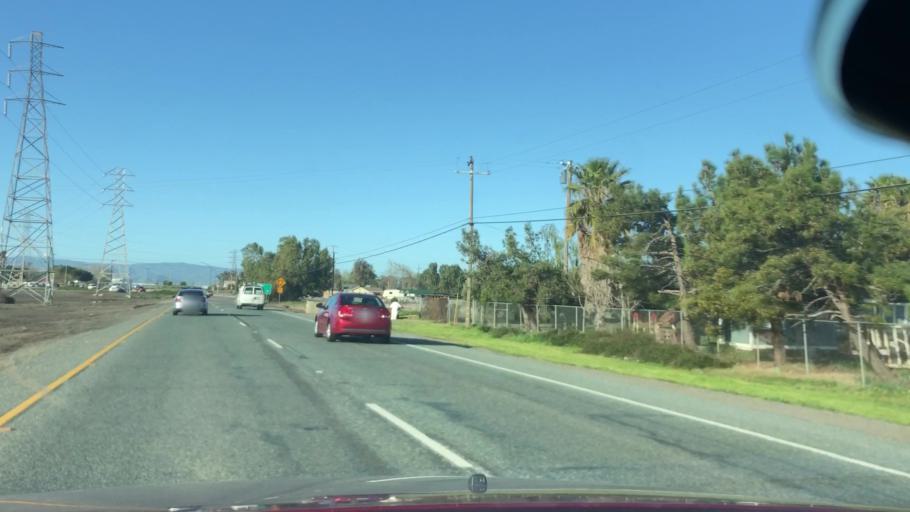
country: US
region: California
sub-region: San Joaquin County
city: Tracy
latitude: 37.7552
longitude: -121.3491
